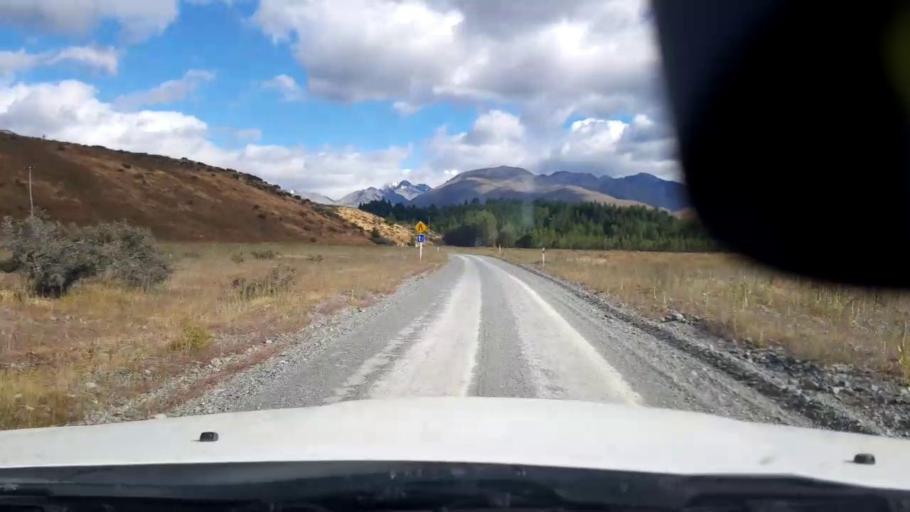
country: NZ
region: Canterbury
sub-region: Timaru District
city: Pleasant Point
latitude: -43.8789
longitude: 170.4665
